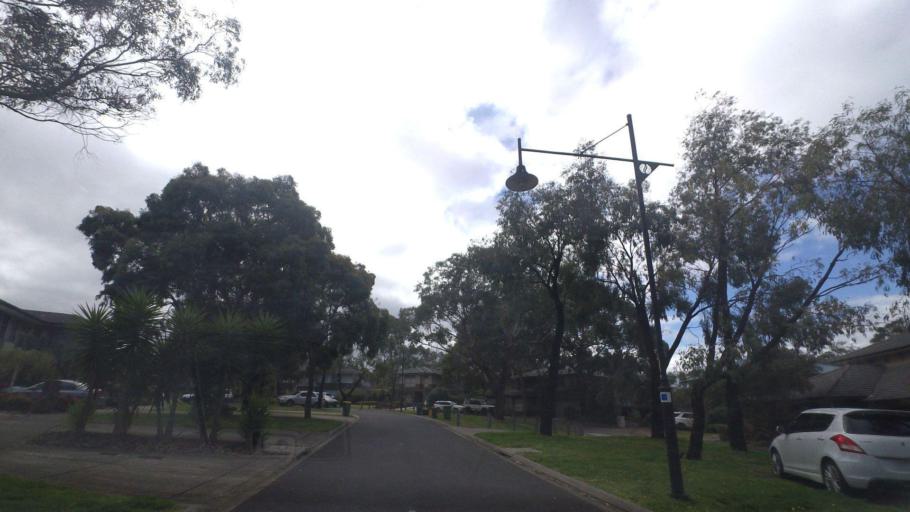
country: AU
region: Victoria
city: Macleod
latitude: -37.7187
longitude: 145.0642
